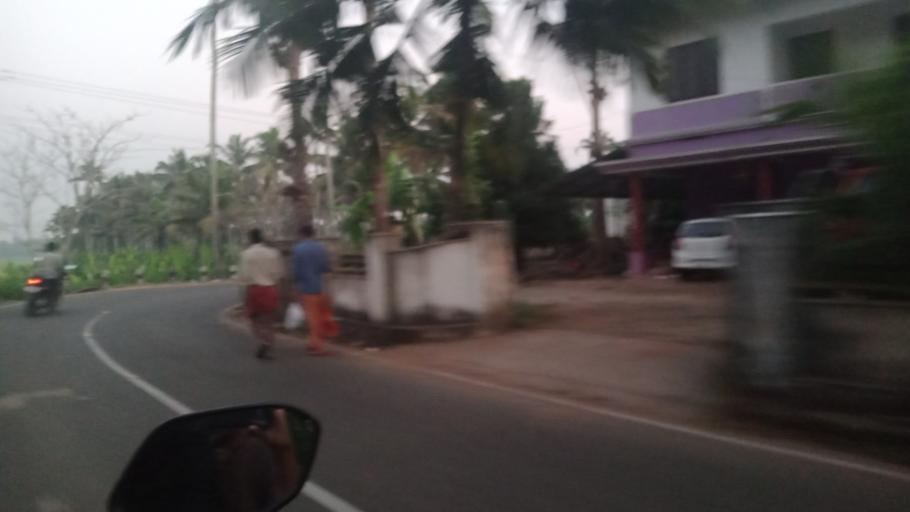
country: IN
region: Kerala
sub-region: Ernakulam
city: Angamali
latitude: 10.2000
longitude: 76.3070
